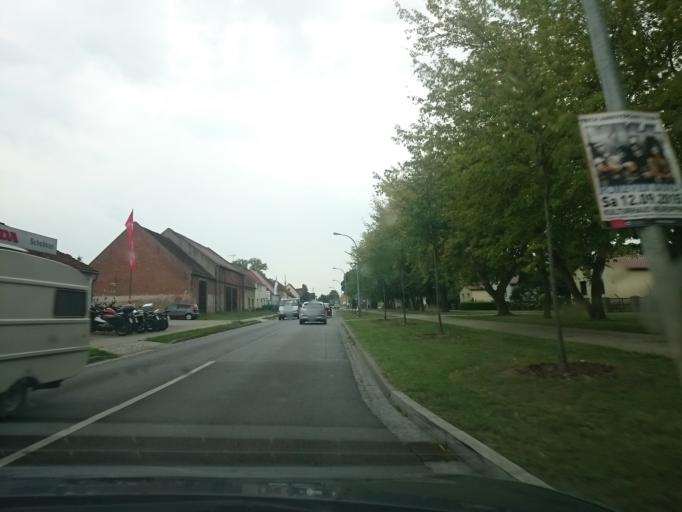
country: DE
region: Brandenburg
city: Gransee
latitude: 53.0086
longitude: 13.1676
